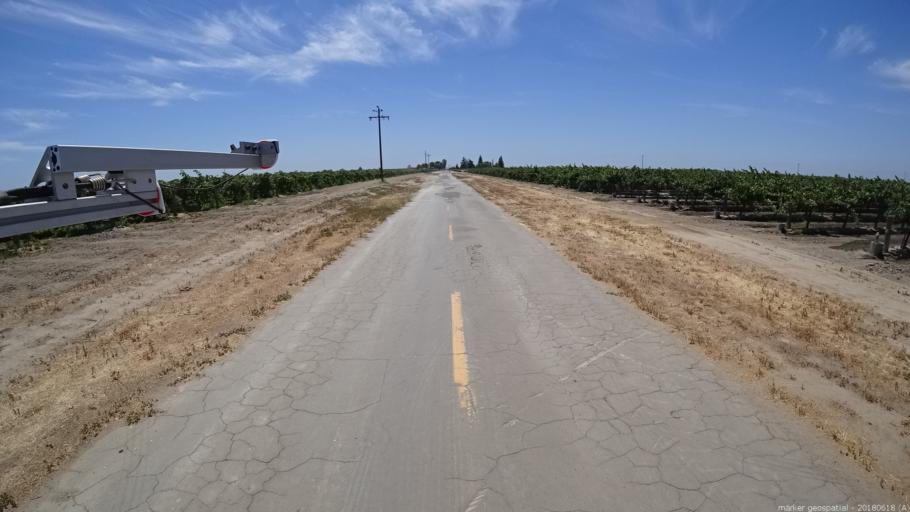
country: US
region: California
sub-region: Madera County
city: Parkwood
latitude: 36.8966
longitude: -120.1196
